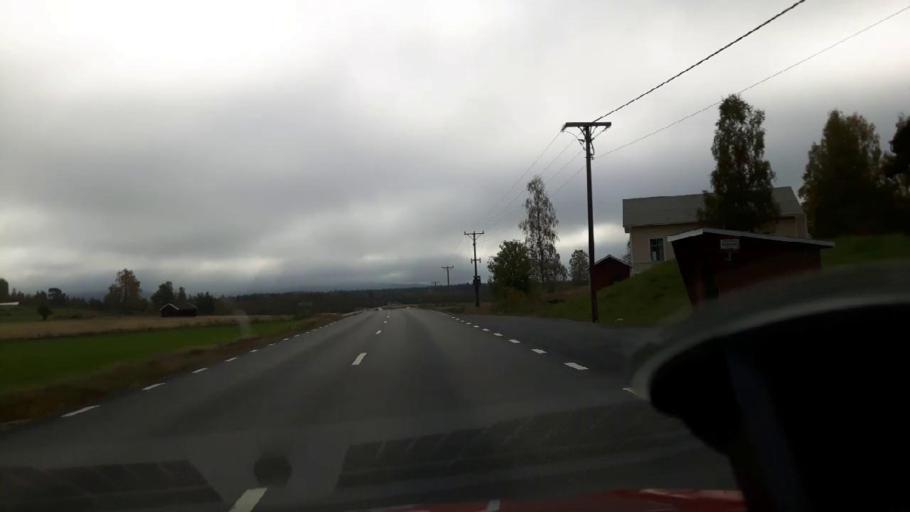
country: SE
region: Gaevleborg
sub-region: Ljusdals Kommun
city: Farila
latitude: 61.8674
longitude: 15.7314
